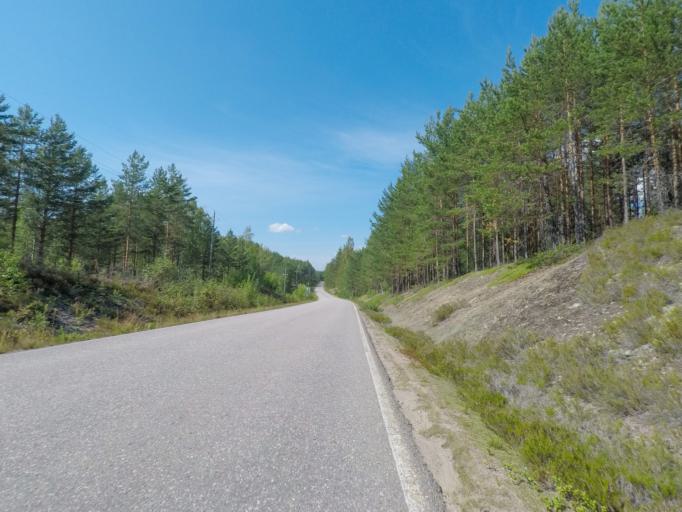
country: FI
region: Southern Savonia
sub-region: Mikkeli
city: Puumala
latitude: 61.4614
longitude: 28.1752
